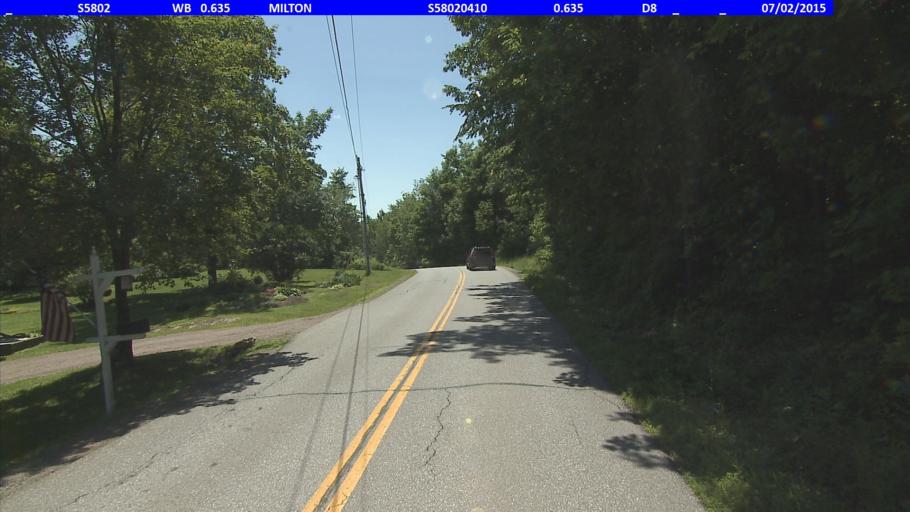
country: US
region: Vermont
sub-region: Chittenden County
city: Colchester
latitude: 44.6170
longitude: -73.2033
